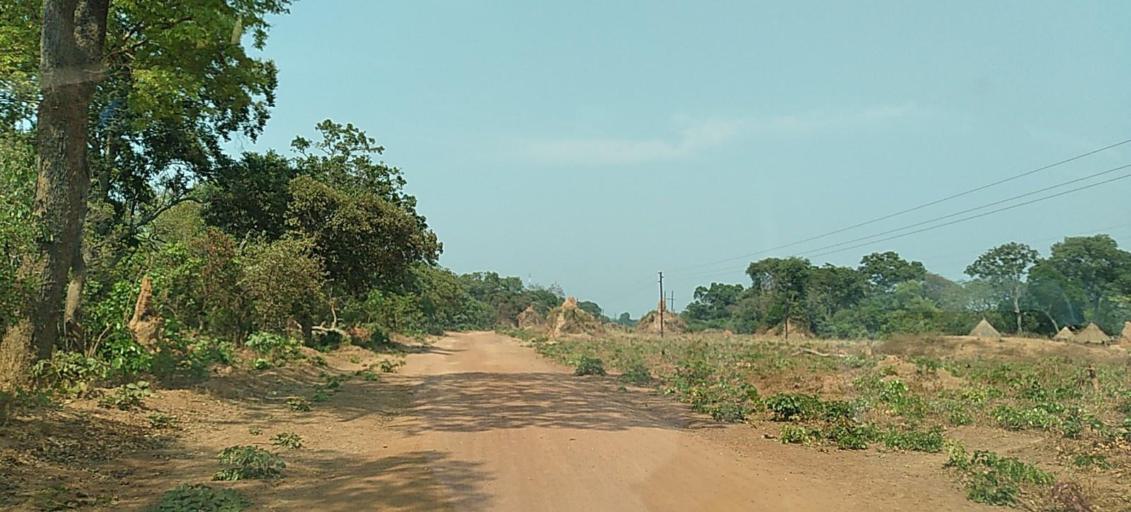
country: ZM
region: Copperbelt
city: Chingola
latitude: -13.0427
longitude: 27.4417
